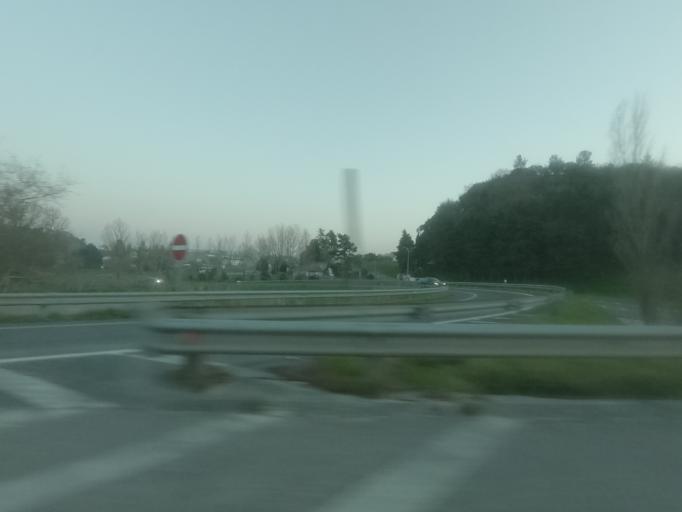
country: PT
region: Leiria
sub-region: Leiria
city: Leiria
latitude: 39.7466
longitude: -8.8266
